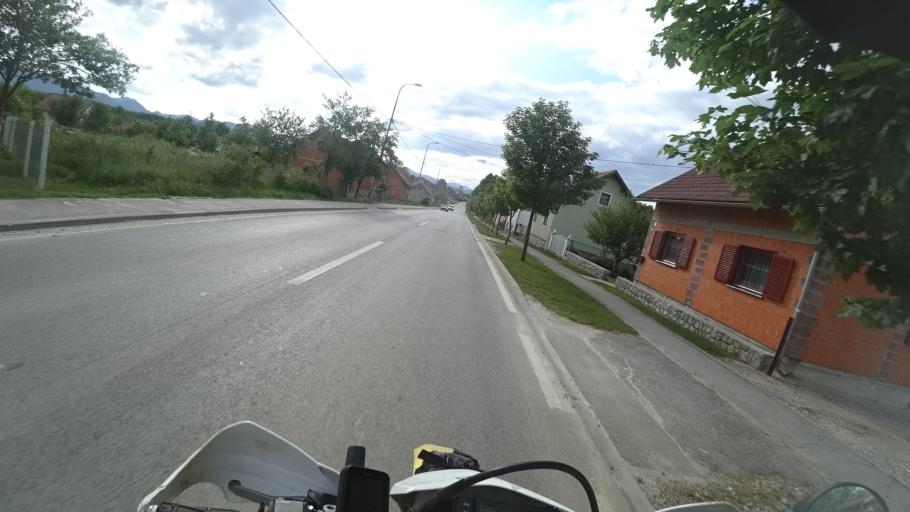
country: HR
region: Licko-Senjska
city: Gospic
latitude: 44.5369
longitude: 15.3901
